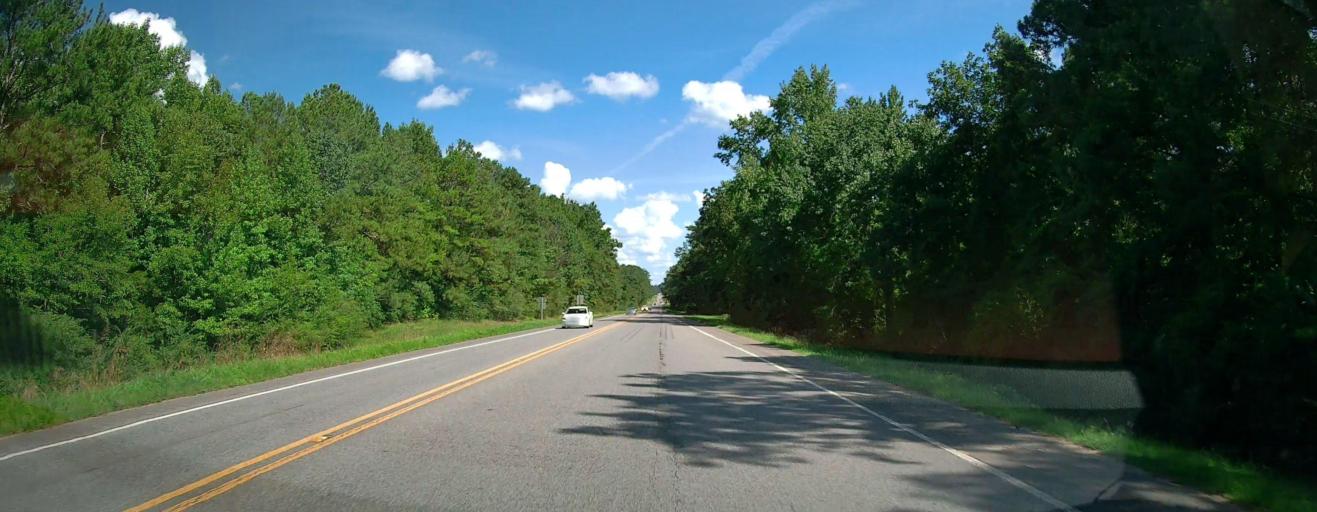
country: US
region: Alabama
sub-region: Pickens County
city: Gordo
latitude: 33.3098
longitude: -87.8900
